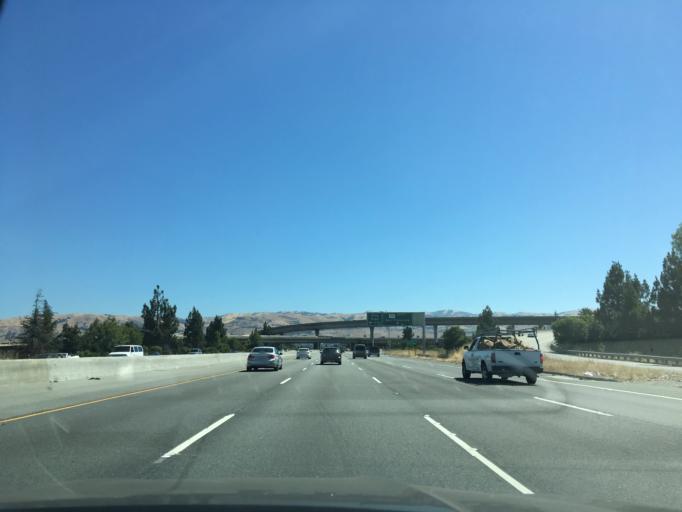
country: US
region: California
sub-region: Santa Clara County
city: San Jose
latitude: 37.3373
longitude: -121.8555
